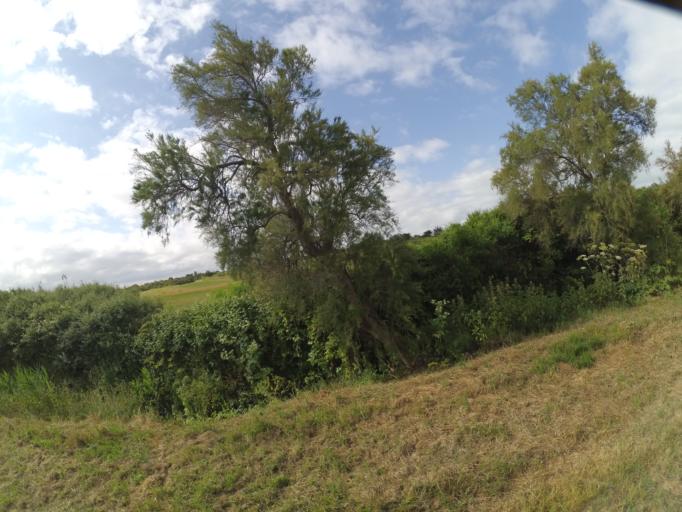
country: FR
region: Poitou-Charentes
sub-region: Departement de la Charente-Maritime
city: Angoulins
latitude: 46.1102
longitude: -1.1194
